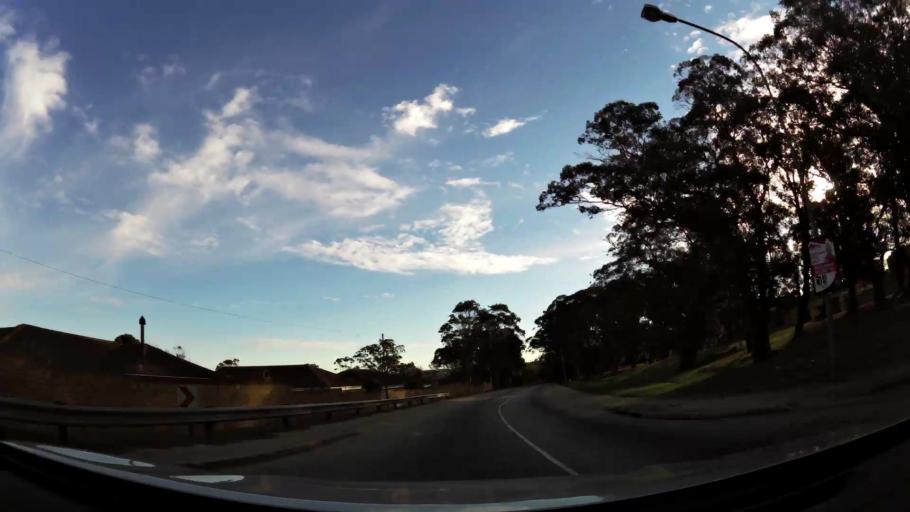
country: ZA
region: Eastern Cape
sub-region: Nelson Mandela Bay Metropolitan Municipality
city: Port Elizabeth
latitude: -33.9558
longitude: 25.5187
